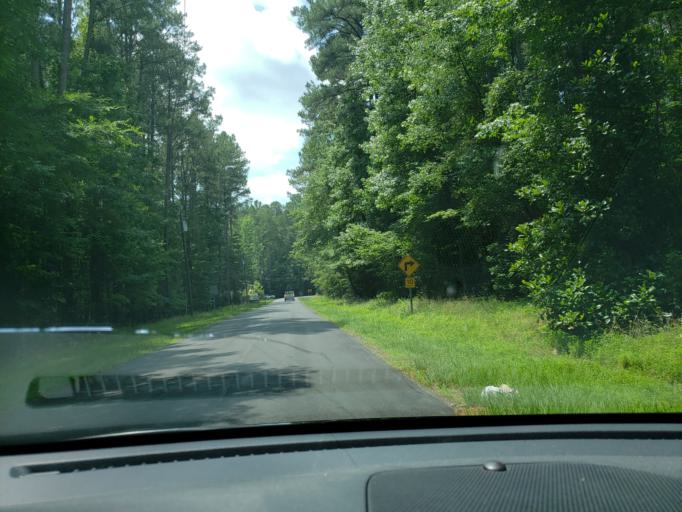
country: US
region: North Carolina
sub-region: Orange County
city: Chapel Hill
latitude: 35.9880
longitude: -78.9975
